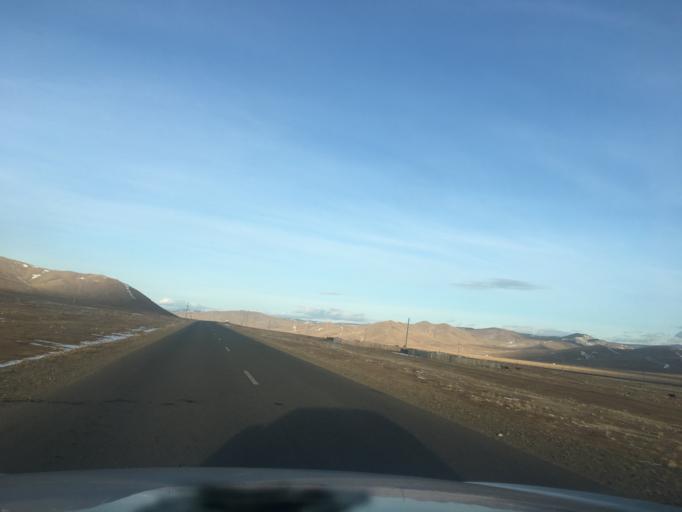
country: MN
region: Central Aimak
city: Mandal
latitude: 48.1058
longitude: 106.6283
